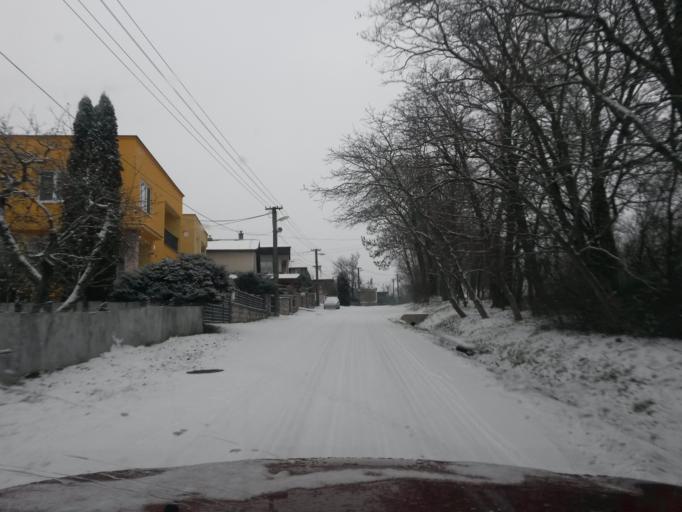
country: SK
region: Kosicky
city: Moldava nad Bodvou
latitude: 48.5988
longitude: 21.0225
